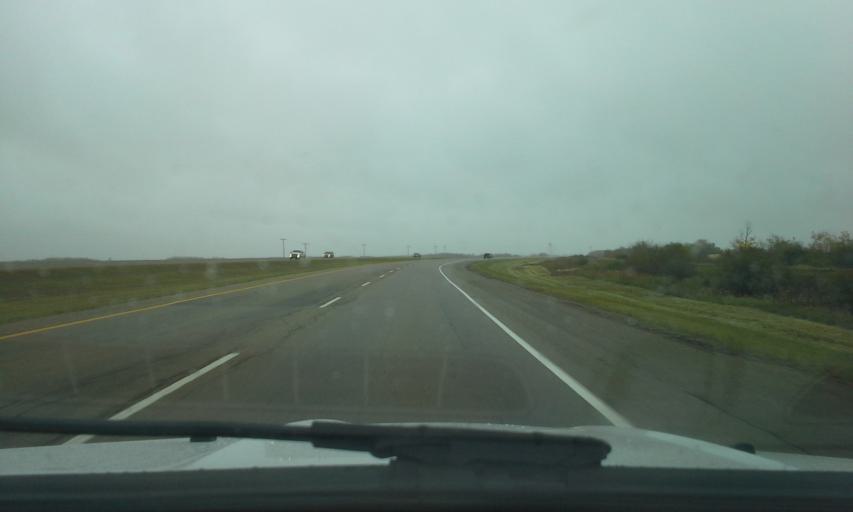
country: CA
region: Saskatchewan
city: Lloydminster
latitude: 53.2279
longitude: -109.8270
